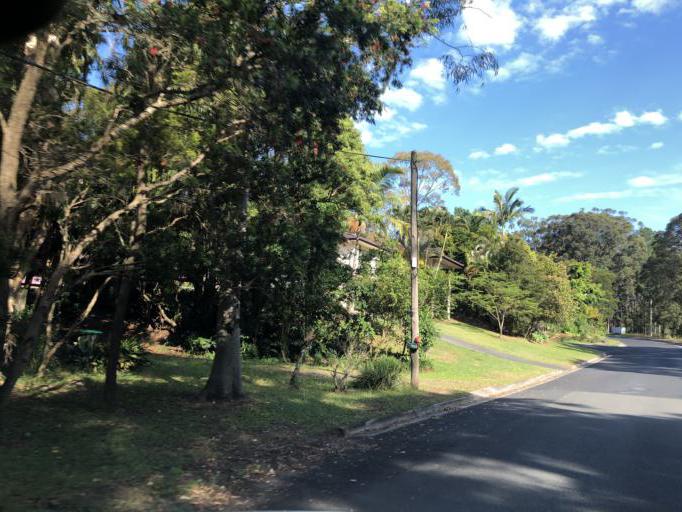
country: AU
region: New South Wales
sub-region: Coffs Harbour
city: Coffs Harbour
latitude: -30.2573
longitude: 153.1311
